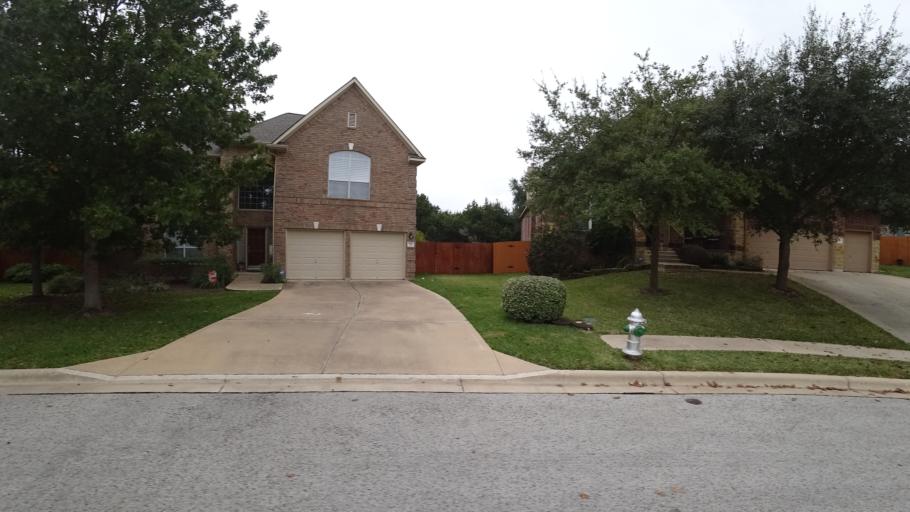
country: US
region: Texas
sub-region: Travis County
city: Bee Cave
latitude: 30.3541
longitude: -97.9019
